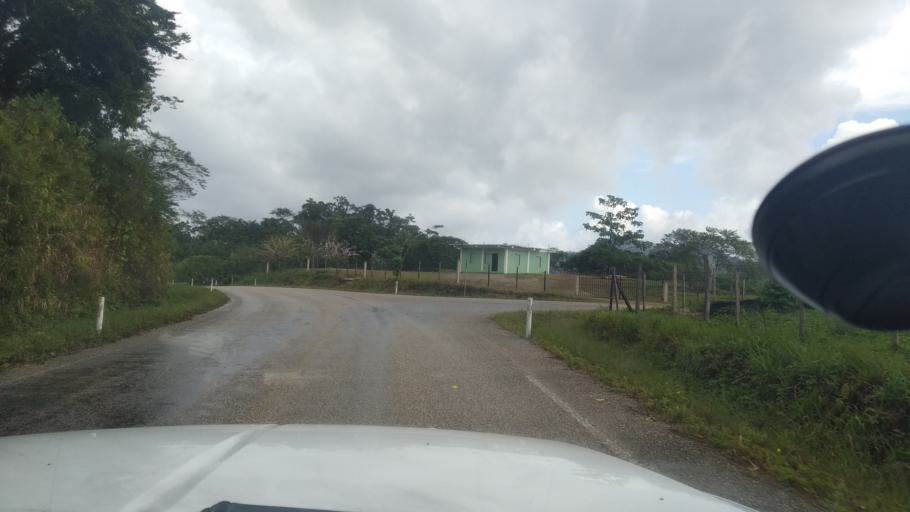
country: GT
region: Peten
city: San Luis
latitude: 16.1989
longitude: -89.1515
